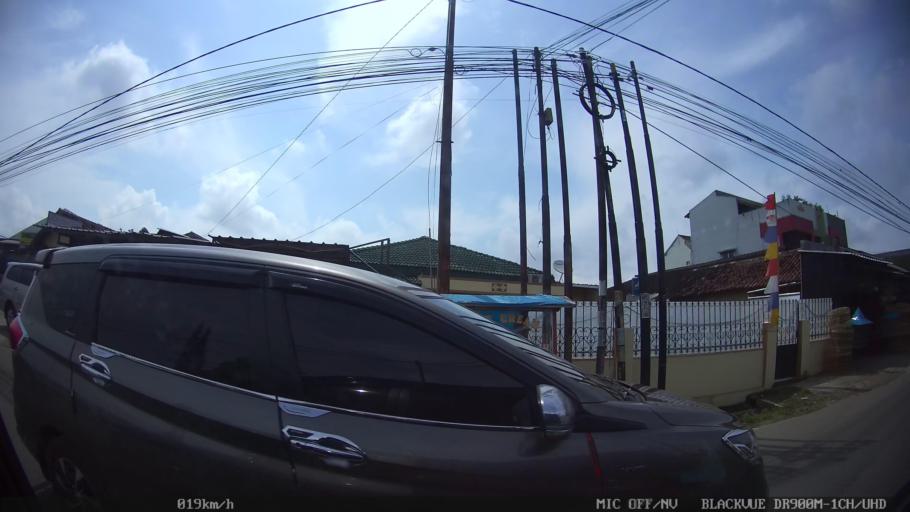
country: ID
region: Lampung
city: Kedaton
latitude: -5.3696
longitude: 105.2748
